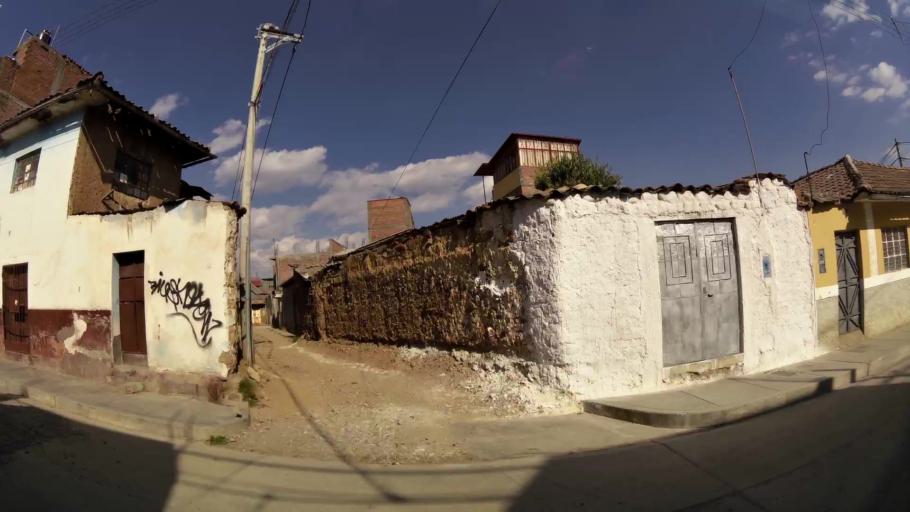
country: PE
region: Junin
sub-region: Provincia de Huancayo
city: El Tambo
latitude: -12.0610
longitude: -75.2191
